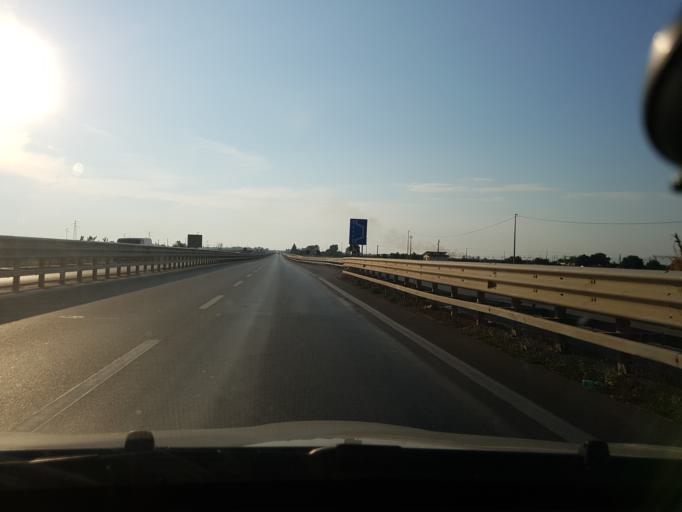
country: IT
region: Apulia
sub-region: Provincia di Foggia
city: Orta Nova
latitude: 41.3492
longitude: 15.7300
